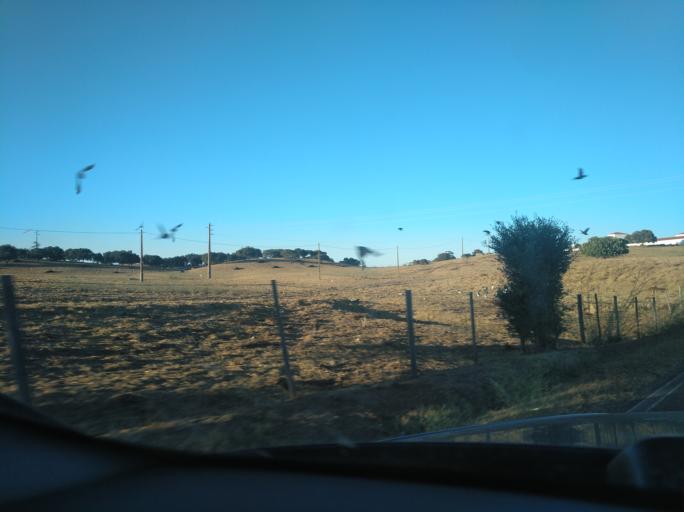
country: PT
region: Portalegre
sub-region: Arronches
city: Arronches
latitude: 39.0680
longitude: -7.2653
